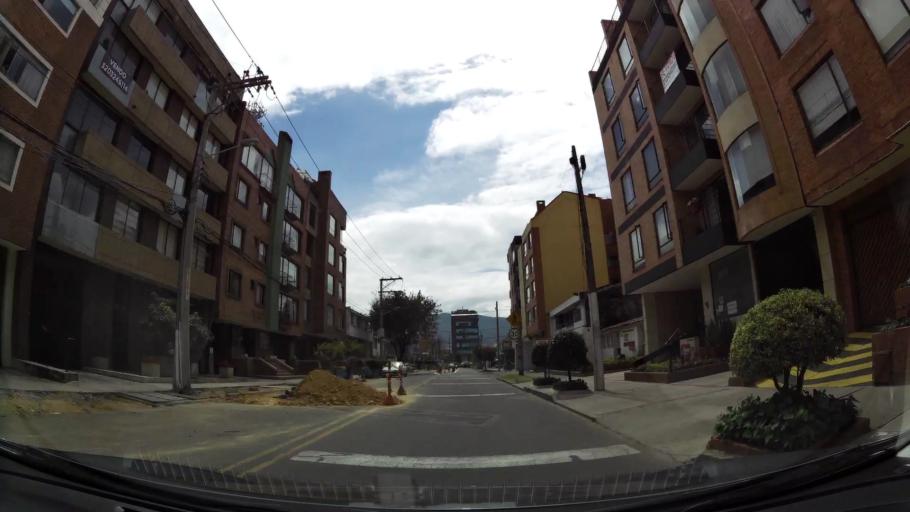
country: CO
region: Bogota D.C.
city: Barrio San Luis
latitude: 4.7032
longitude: -74.0563
